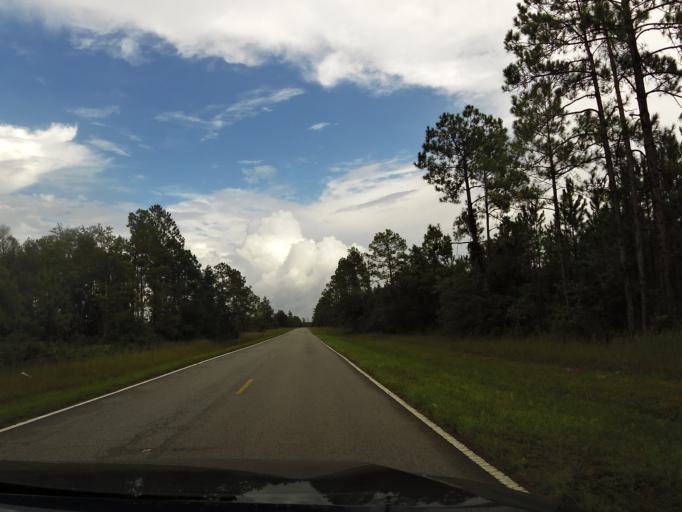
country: US
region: Florida
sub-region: Duval County
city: Baldwin
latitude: 30.4012
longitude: -81.9692
